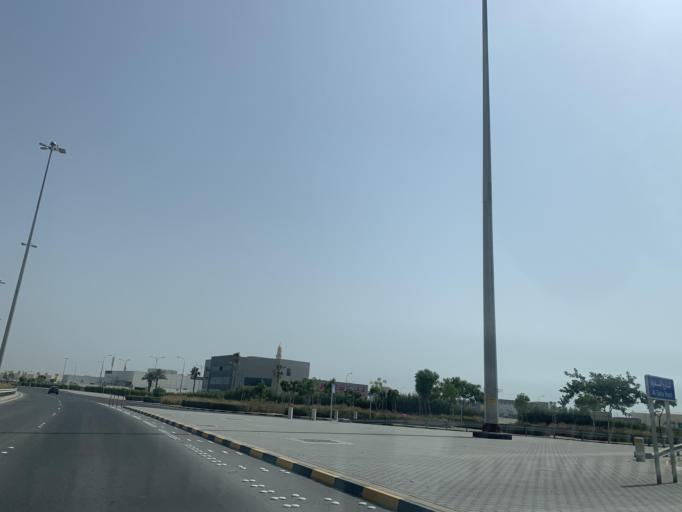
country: BH
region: Muharraq
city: Al Muharraq
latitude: 26.3084
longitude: 50.6396
